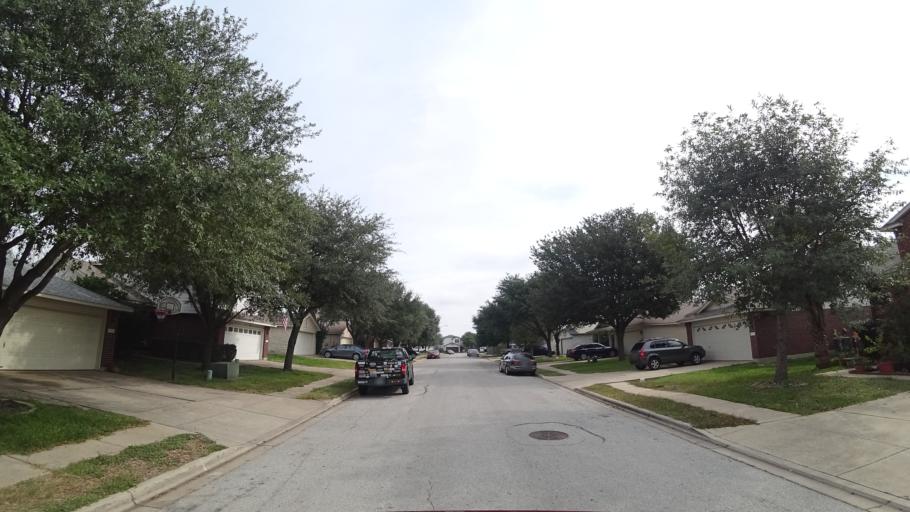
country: US
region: Texas
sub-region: Travis County
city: Windemere
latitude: 30.4462
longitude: -97.6547
